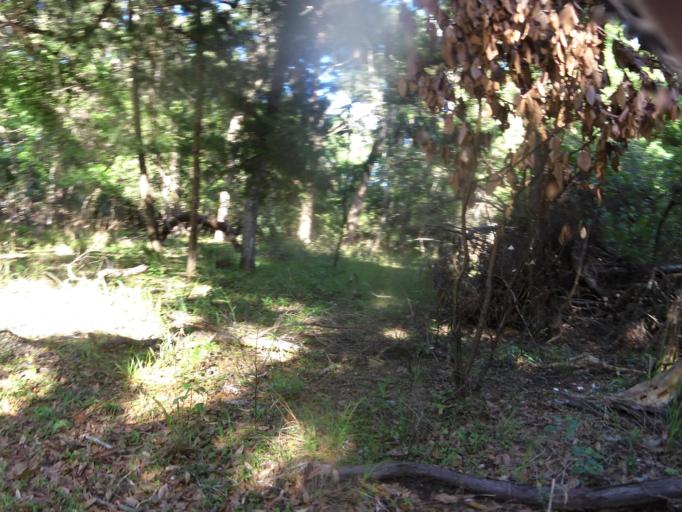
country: US
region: Florida
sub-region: Saint Johns County
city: Villano Beach
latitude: 30.0102
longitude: -81.3305
